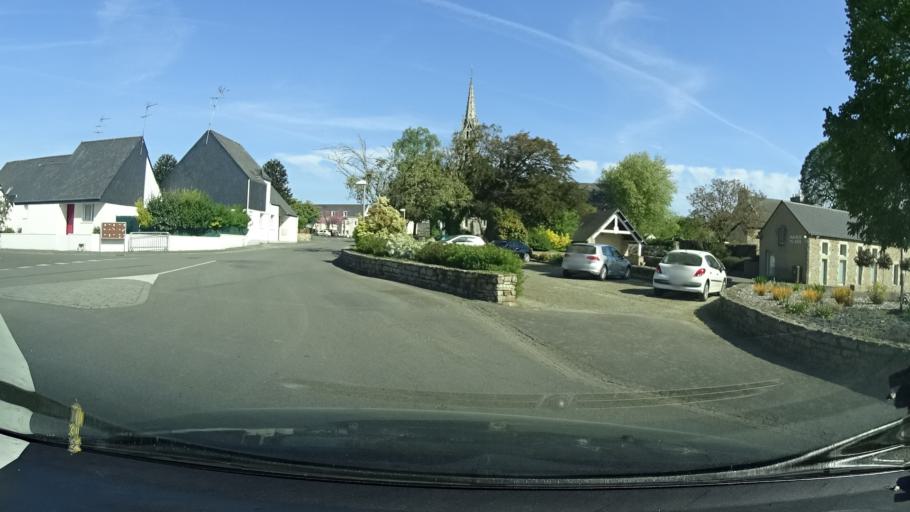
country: FR
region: Brittany
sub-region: Departement du Finistere
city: Mellac
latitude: 47.9032
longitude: -3.5768
